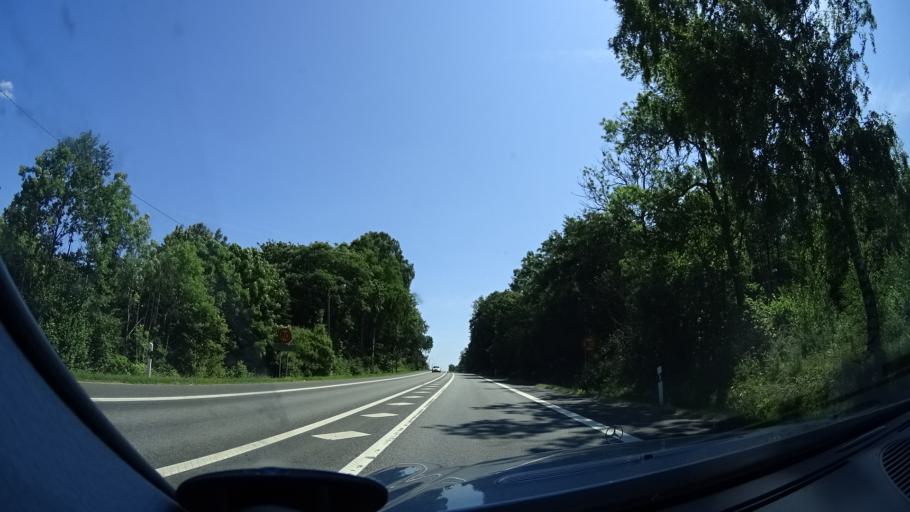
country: SE
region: Skane
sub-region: Kristianstads Kommun
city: Onnestad
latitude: 55.9390
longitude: 13.9082
